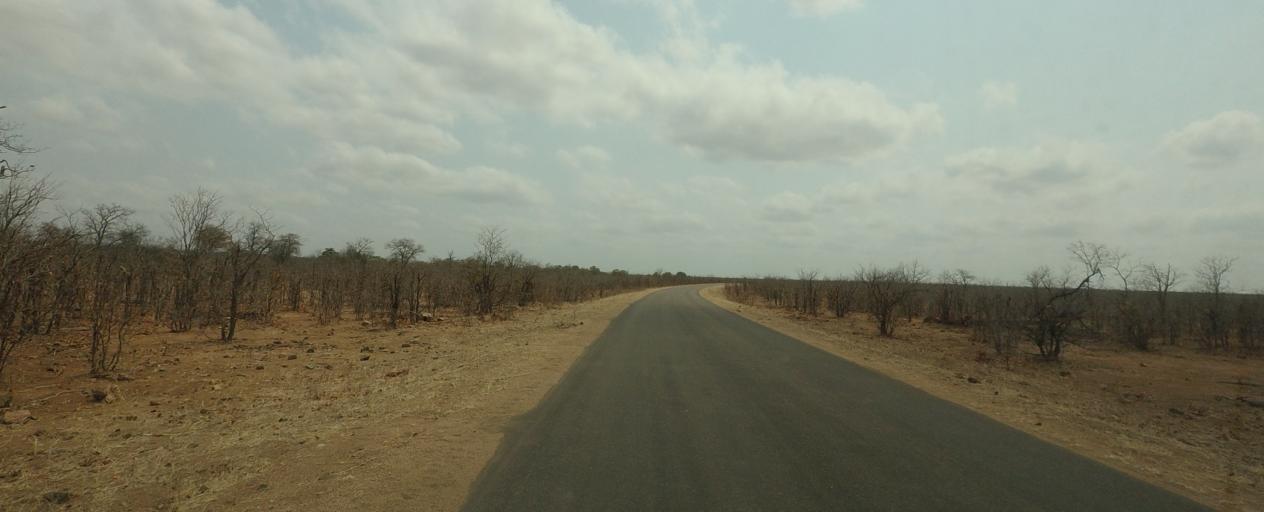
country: ZA
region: Limpopo
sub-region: Mopani District Municipality
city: Phalaborwa
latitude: -23.5485
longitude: 31.4291
